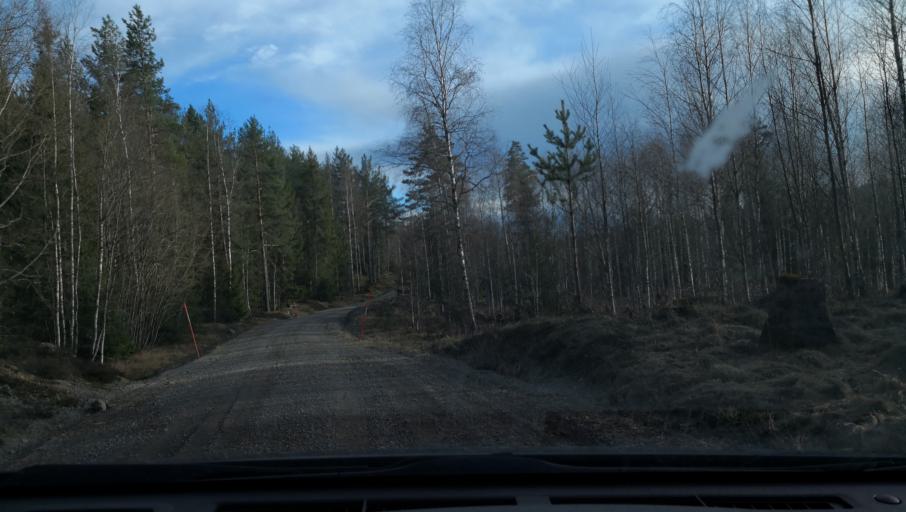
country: SE
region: Vaestmanland
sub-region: Arboga Kommun
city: Arboga
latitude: 59.4400
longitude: 15.7525
